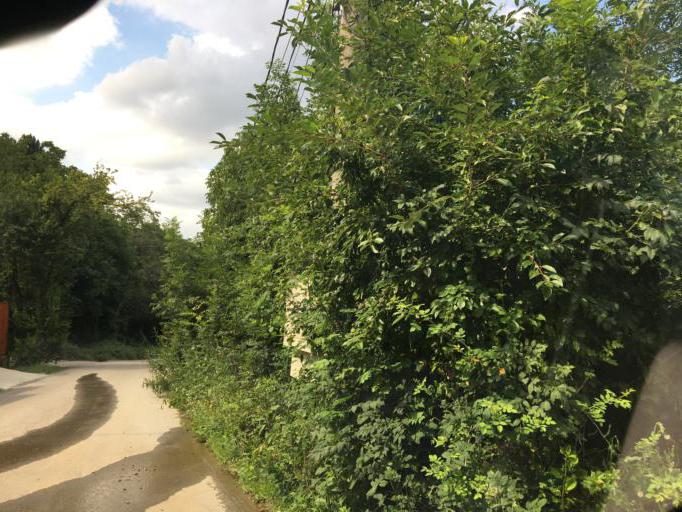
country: BG
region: Sofia-Capital
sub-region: Stolichna Obshtina
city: Sofia
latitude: 42.6078
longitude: 23.3656
